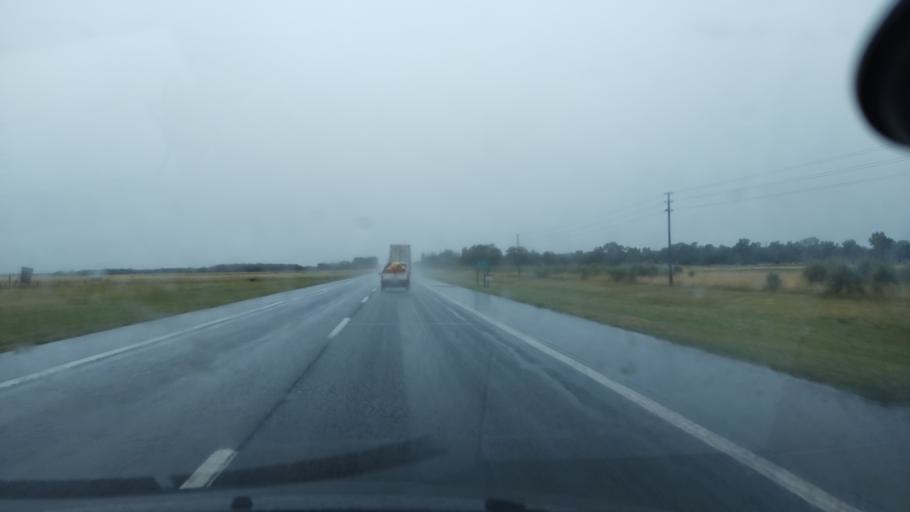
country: AR
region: Buenos Aires
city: Canuelas
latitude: -35.0649
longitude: -58.8231
